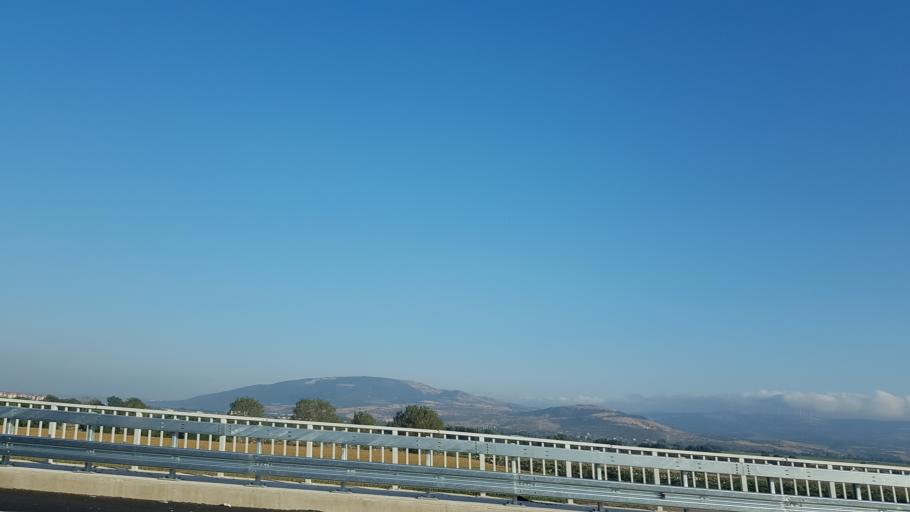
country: TR
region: Bursa
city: Karacabey
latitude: 40.2220
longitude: 28.4018
